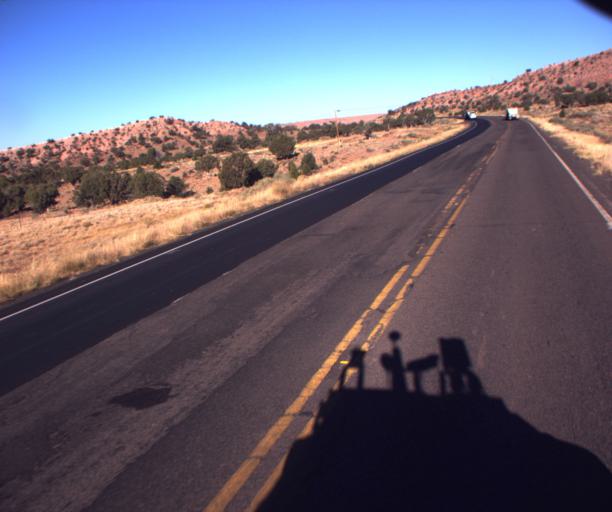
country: US
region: Arizona
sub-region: Apache County
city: Ganado
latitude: 35.7408
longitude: -109.6103
